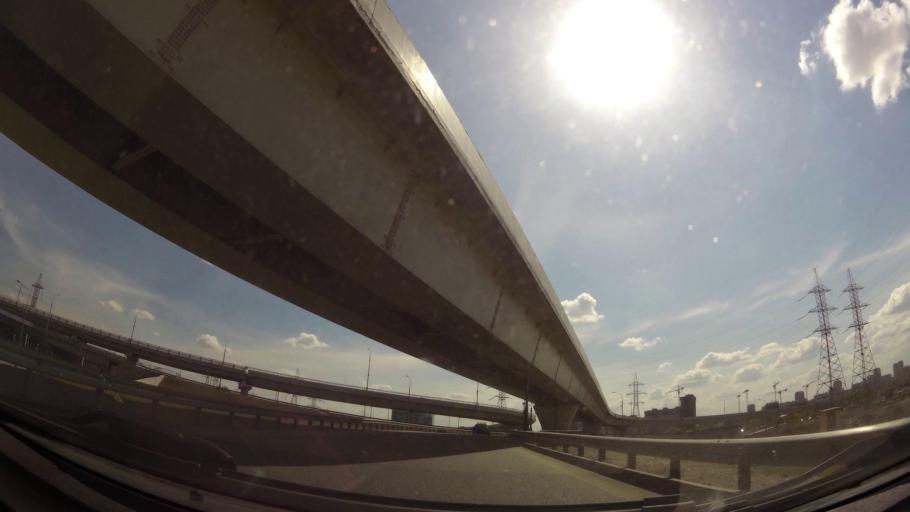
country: RU
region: Moskovskaya
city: Vostryakovo
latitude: 55.6629
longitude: 37.4305
